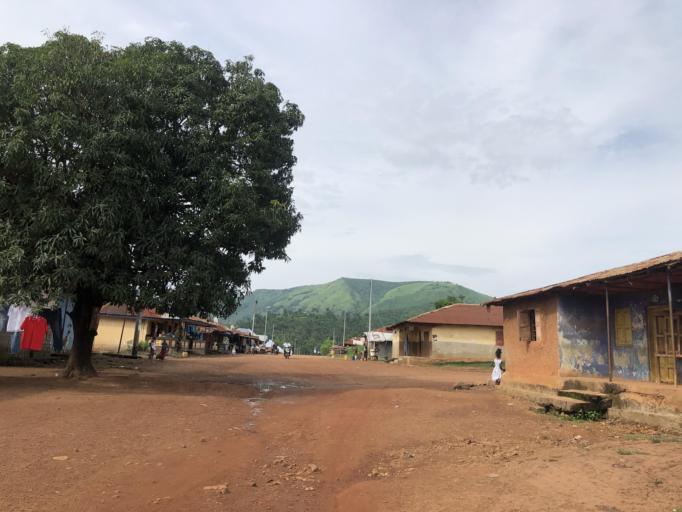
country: SL
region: Northern Province
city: Bumbuna
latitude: 9.0437
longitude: -11.7458
